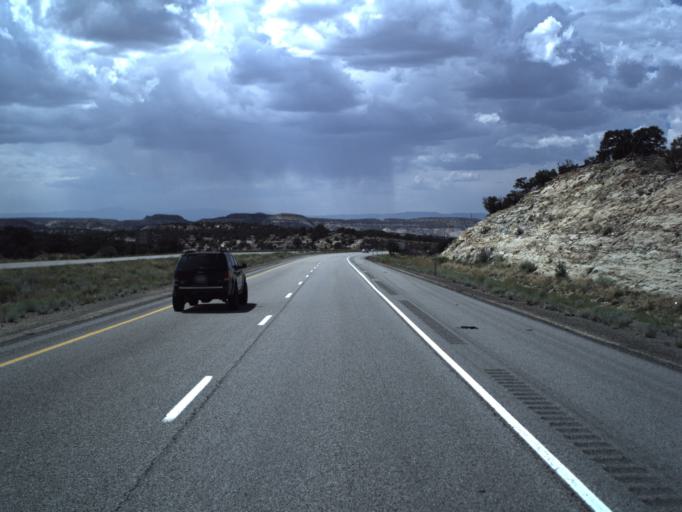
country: US
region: Utah
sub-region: Emery County
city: Ferron
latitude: 38.8591
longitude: -110.8317
